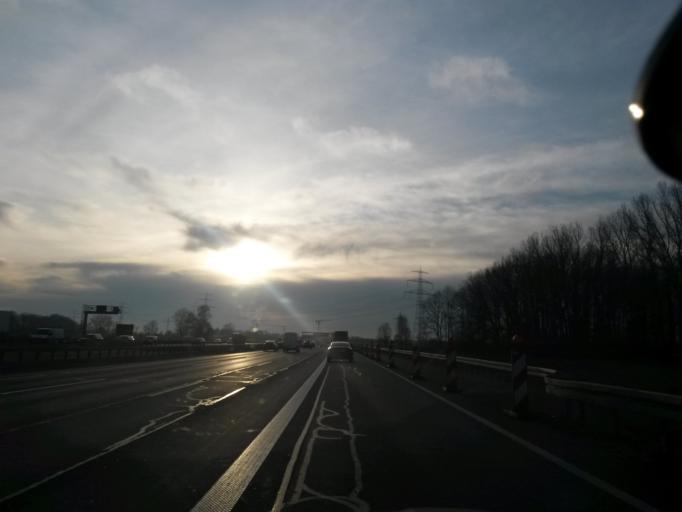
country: DE
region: Bavaria
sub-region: Upper Bavaria
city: Ismaning
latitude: 48.1956
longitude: 11.6811
